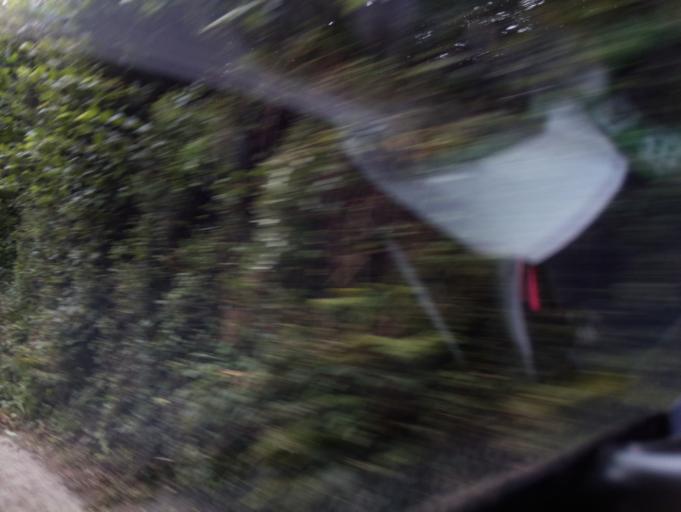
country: GB
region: England
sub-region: Devon
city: Totnes
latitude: 50.3430
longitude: -3.6844
